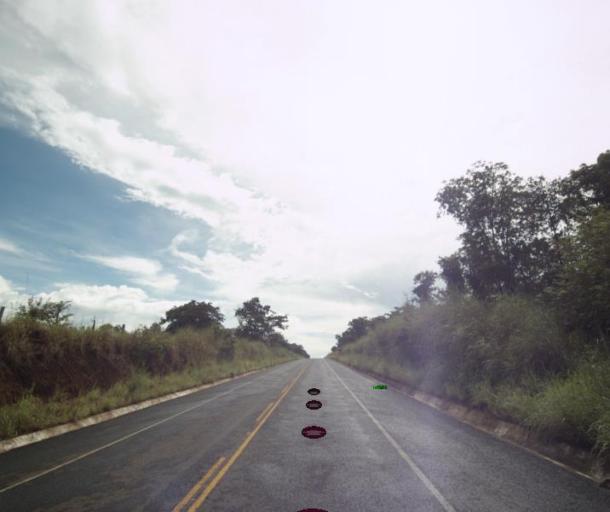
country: BR
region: Goias
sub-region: Sao Miguel Do Araguaia
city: Sao Miguel do Araguaia
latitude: -13.3023
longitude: -50.2769
